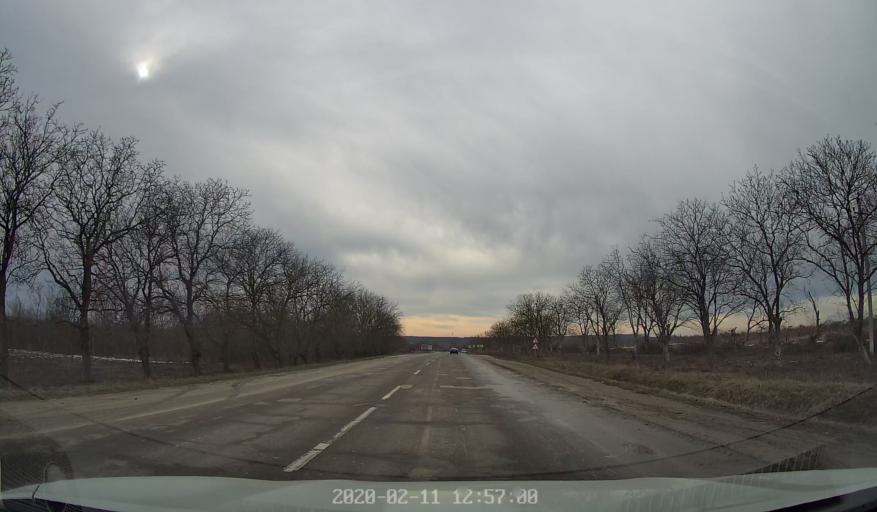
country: MD
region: Briceni
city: Briceni
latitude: 48.3451
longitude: 27.0721
